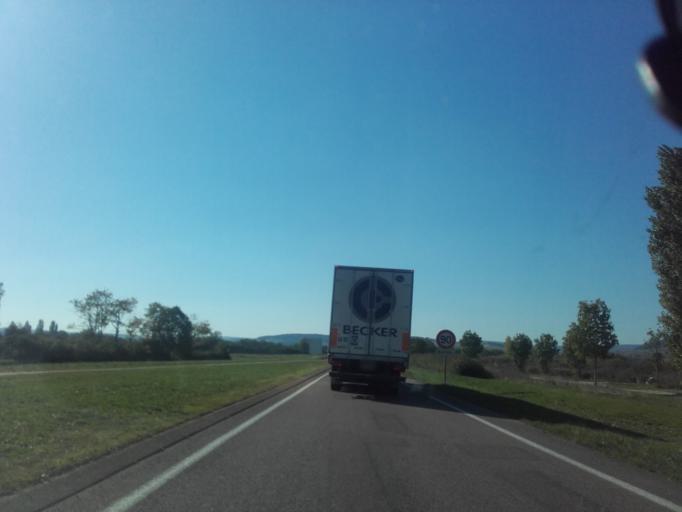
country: FR
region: Bourgogne
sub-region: Departement de la Cote-d'Or
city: Bligny-les-Beaune
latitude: 47.0029
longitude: 4.8392
